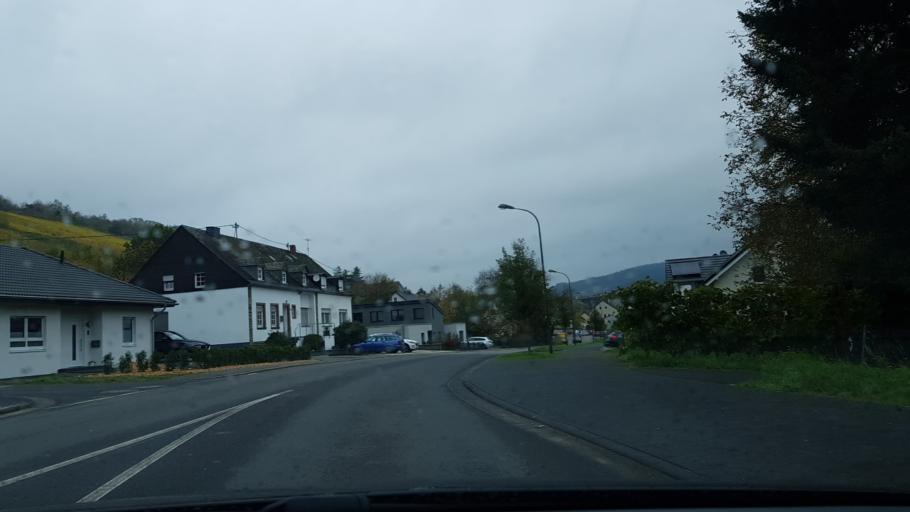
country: DE
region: Rheinland-Pfalz
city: Longuich
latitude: 49.7872
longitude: 6.7726
